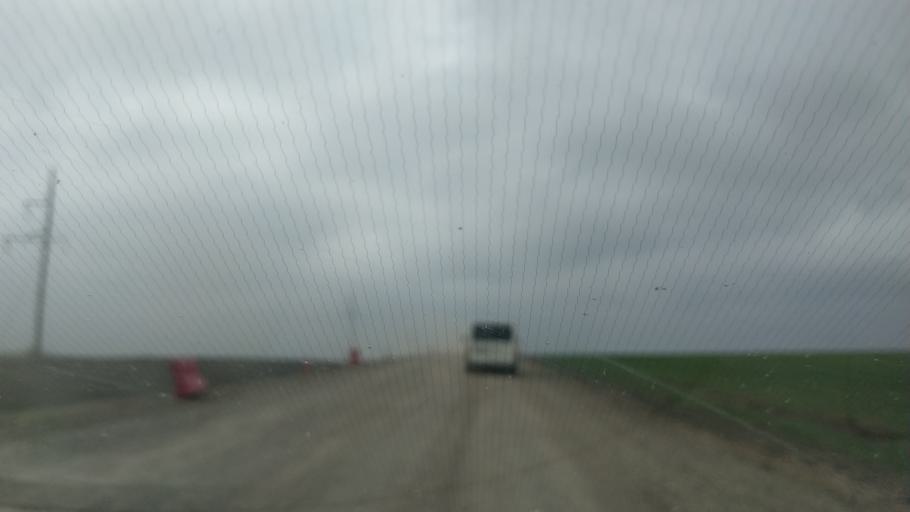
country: MD
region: Gagauzia
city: Bugeac
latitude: 46.3245
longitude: 28.7272
